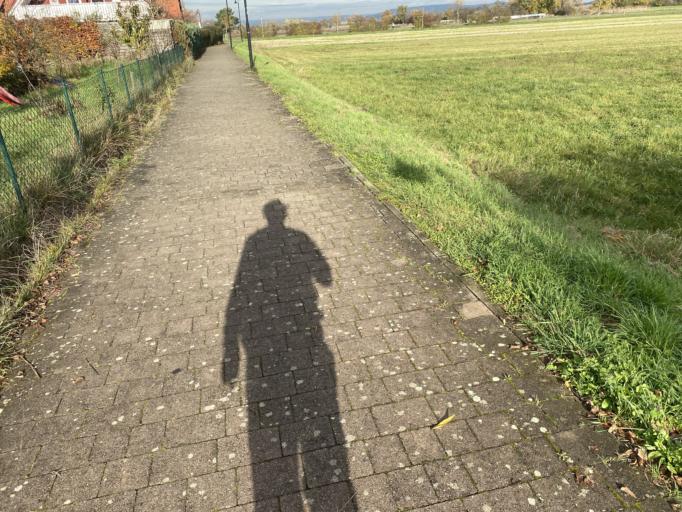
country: DE
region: Bavaria
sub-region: Regierungsbezirk Mittelfranken
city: Baiersdorf
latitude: 49.6553
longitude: 11.0451
